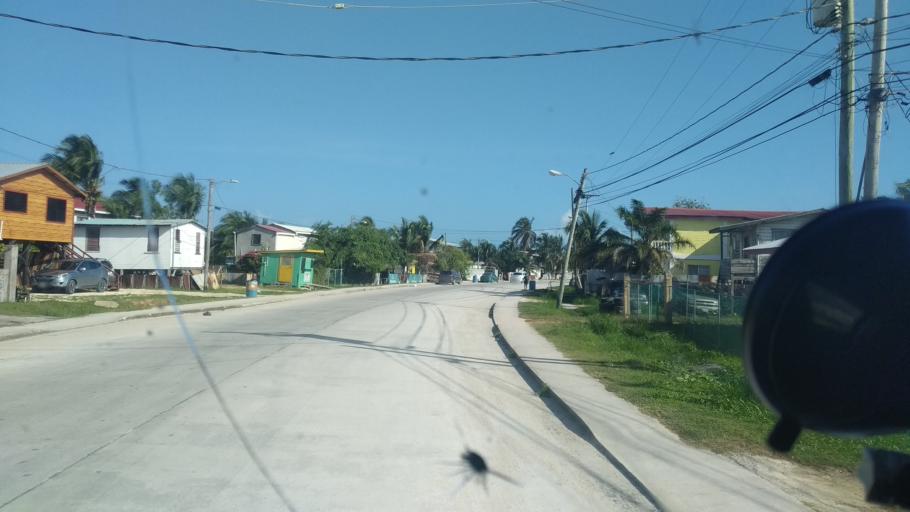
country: BZ
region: Belize
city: Belize City
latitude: 17.4853
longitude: -88.2019
